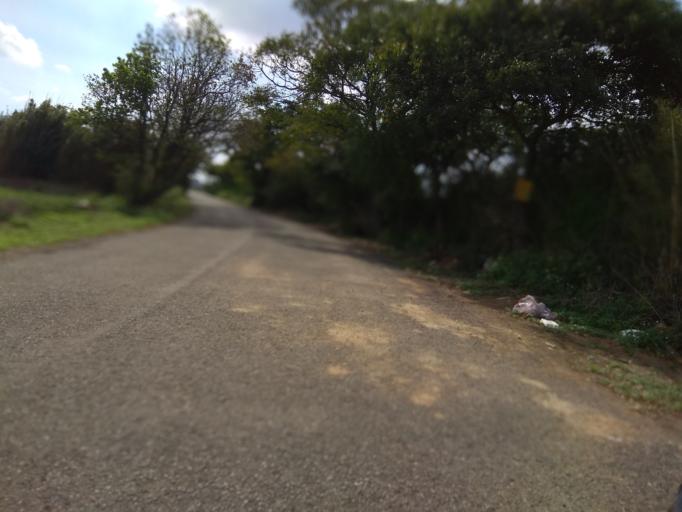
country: TW
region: Taiwan
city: Taoyuan City
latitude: 25.0477
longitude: 121.2282
